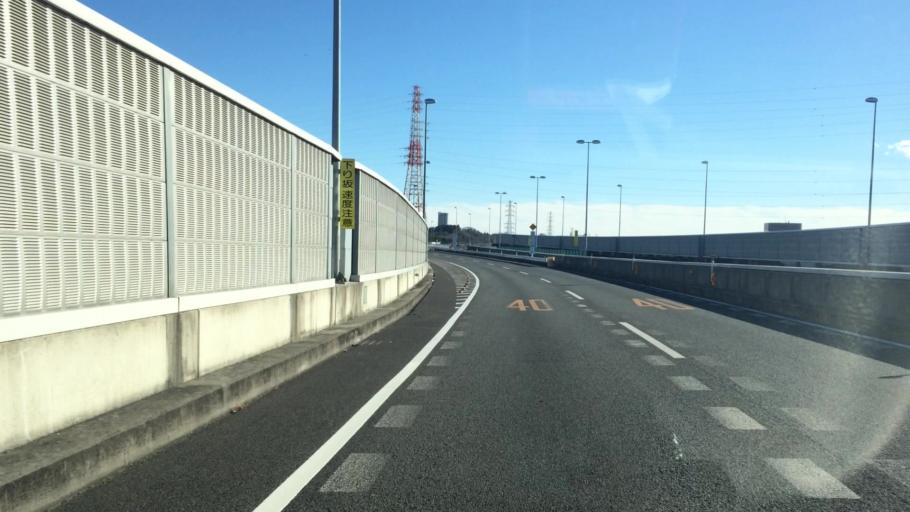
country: JP
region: Tochigi
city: Utsunomiya-shi
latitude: 36.5956
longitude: 139.8650
